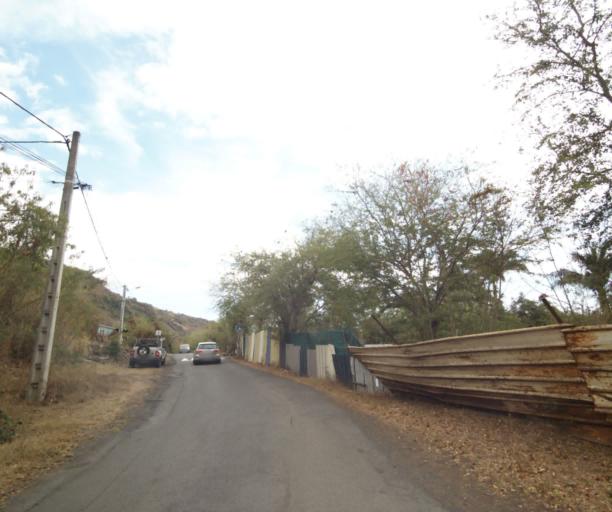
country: RE
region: Reunion
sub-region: Reunion
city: Saint-Paul
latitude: -21.0023
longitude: 55.3005
